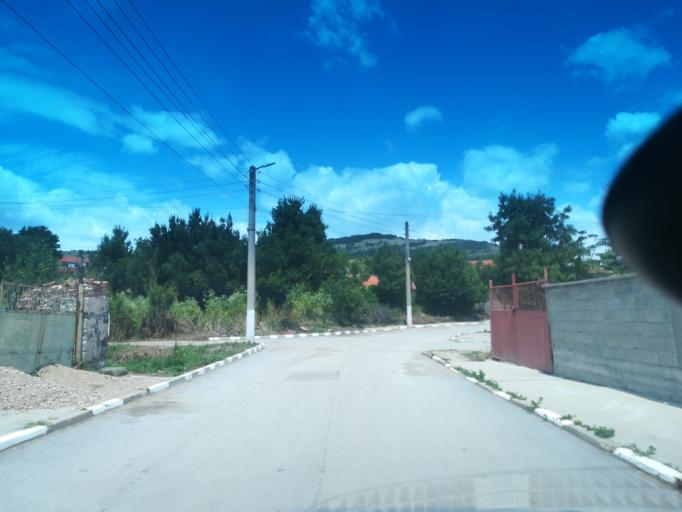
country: BG
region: Khaskovo
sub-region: Obshtina Mineralni Bani
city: Mineralni Bani
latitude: 41.9473
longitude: 25.2460
